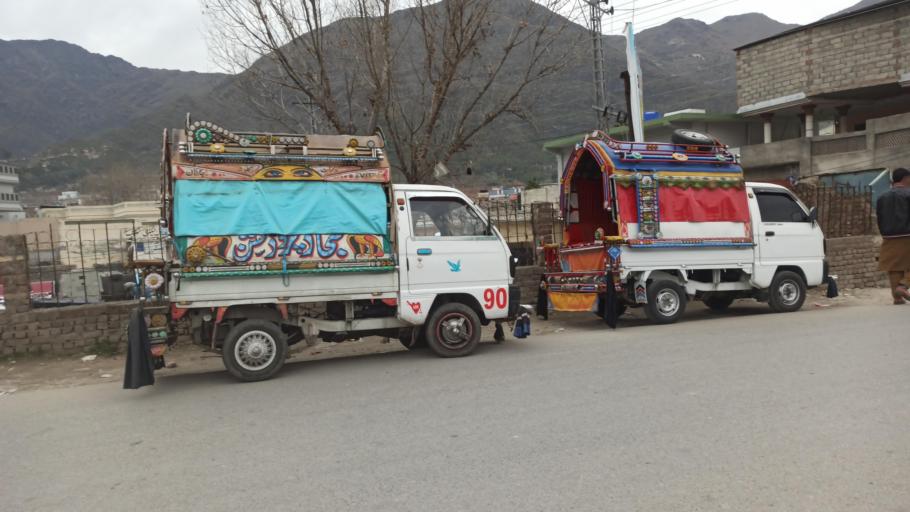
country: PK
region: Khyber Pakhtunkhwa
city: Saidu Sharif
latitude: 34.7399
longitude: 72.3409
